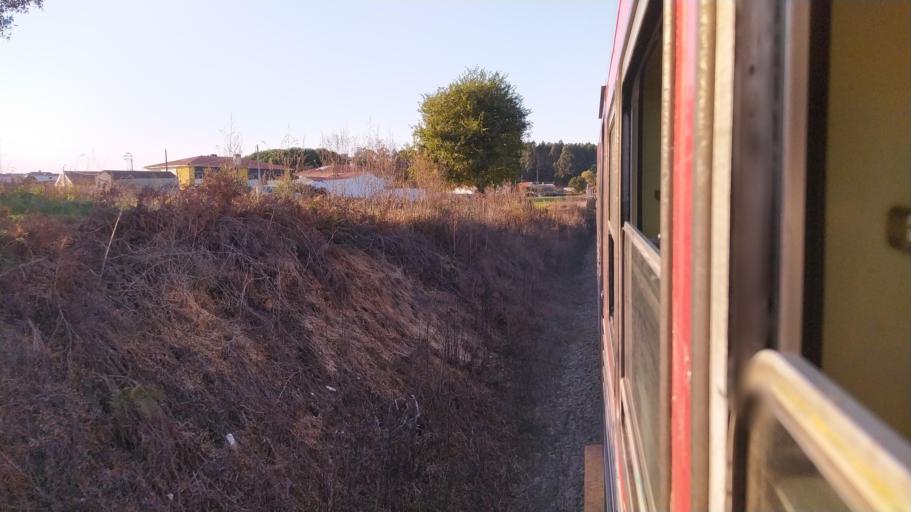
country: PT
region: Aveiro
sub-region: Aveiro
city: Eixo
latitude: 40.6382
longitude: -8.5839
